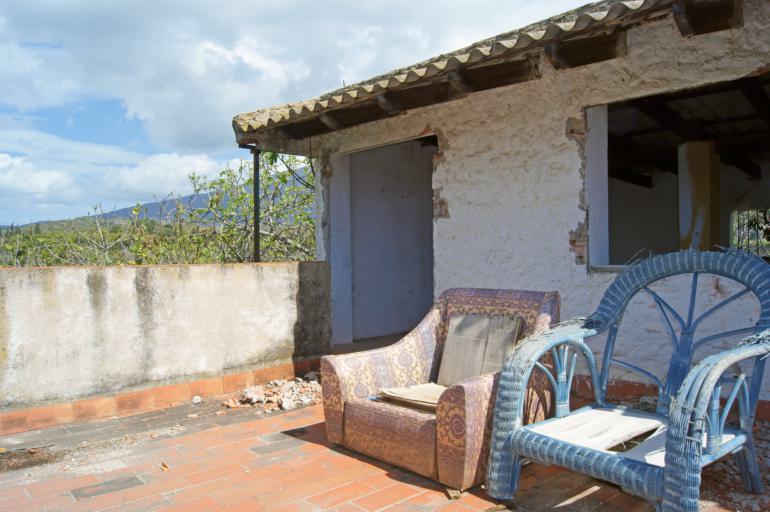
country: ES
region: Andalusia
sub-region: Provincia de Malaga
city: Fuengirola
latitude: 36.5512
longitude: -4.6929
